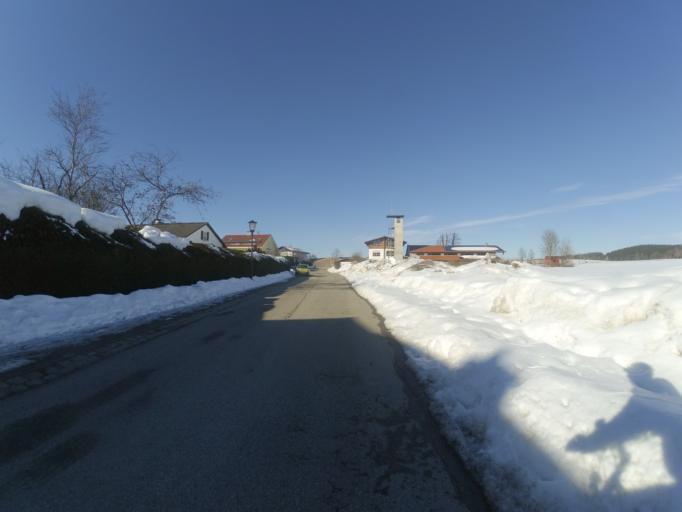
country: DE
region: Bavaria
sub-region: Upper Bavaria
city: Aying
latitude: 47.9443
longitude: 11.7969
